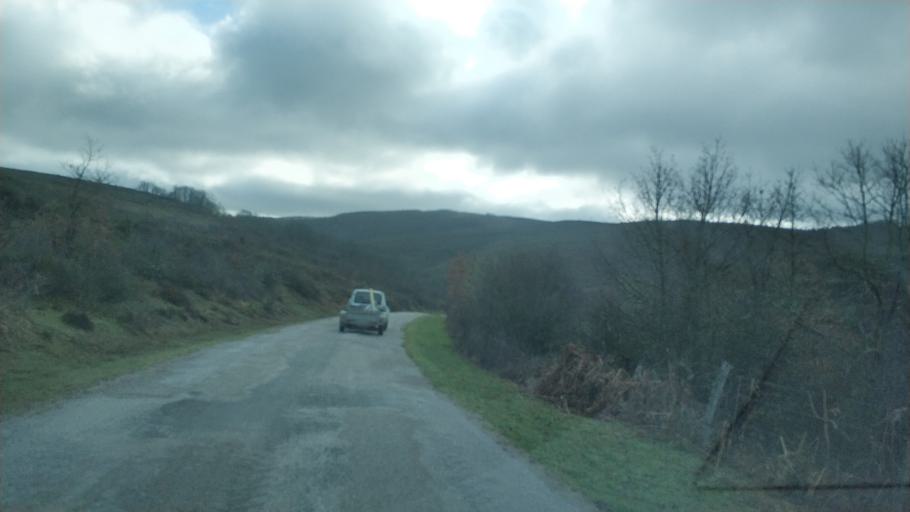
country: ES
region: Castille and Leon
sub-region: Provincia de Burgos
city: Arija
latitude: 42.9134
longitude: -4.0000
